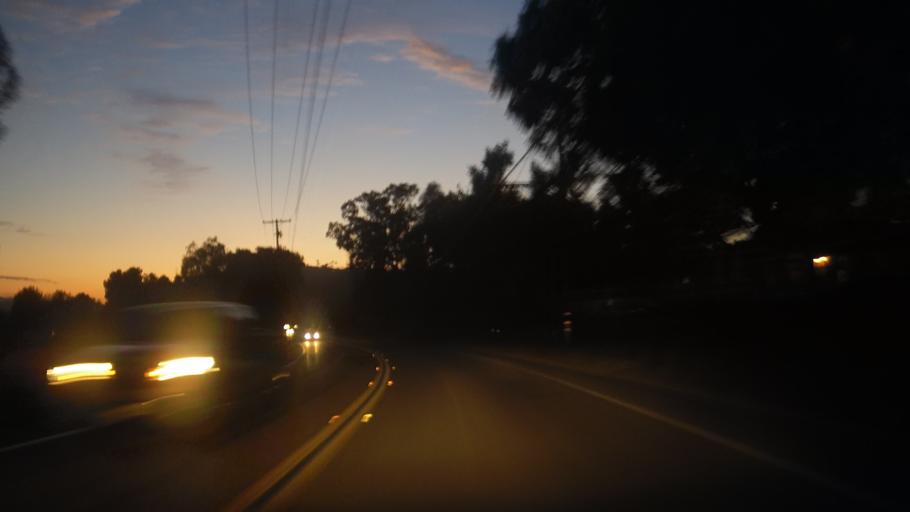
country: US
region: California
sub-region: San Diego County
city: Rancho San Diego
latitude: 32.7600
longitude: -116.8976
